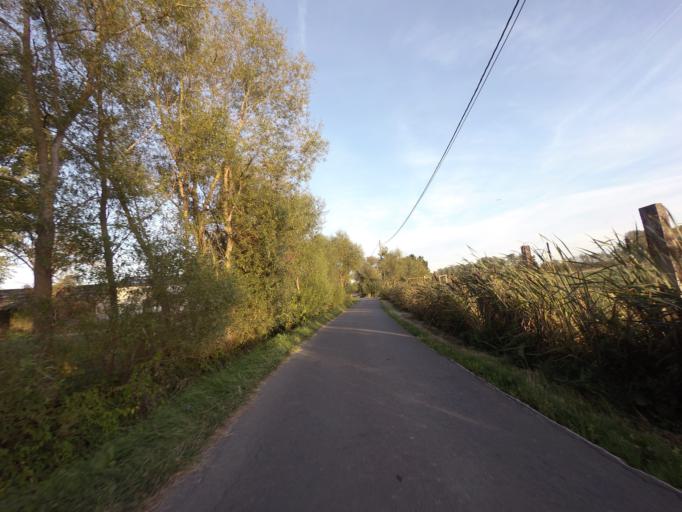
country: BE
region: Flanders
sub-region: Provincie Vlaams-Brabant
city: Haacht
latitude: 50.9461
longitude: 4.6347
